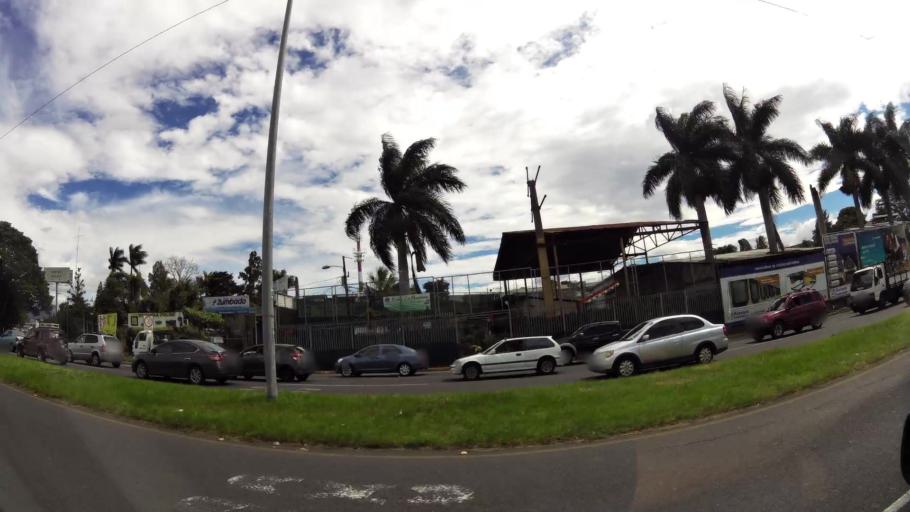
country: CR
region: San Jose
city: San Pedro
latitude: 9.9206
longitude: -84.0606
